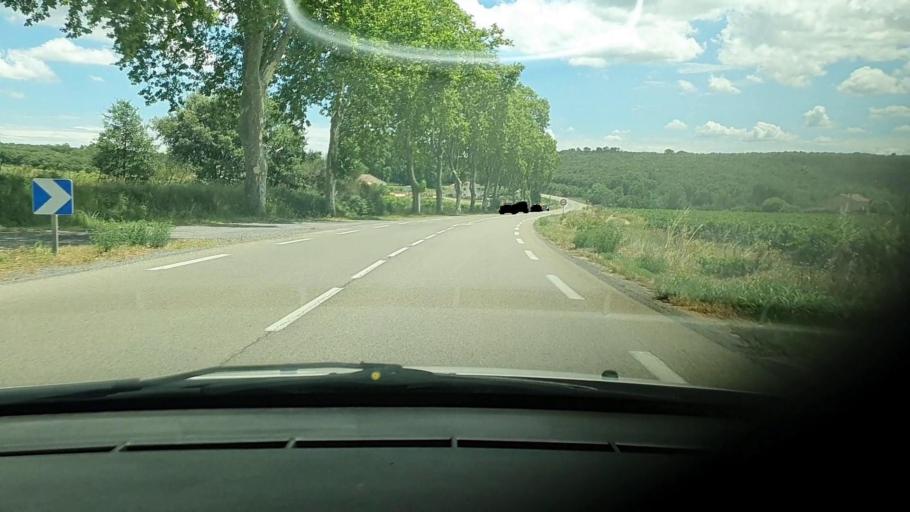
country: FR
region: Languedoc-Roussillon
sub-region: Departement du Gard
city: Moussac
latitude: 44.0611
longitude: 4.2613
